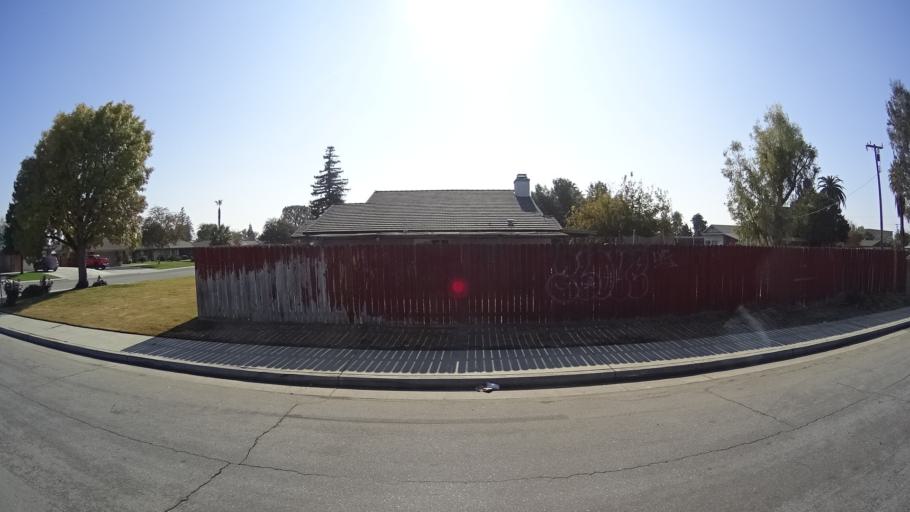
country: US
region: California
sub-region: Kern County
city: Greenfield
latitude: 35.2740
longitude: -119.0196
